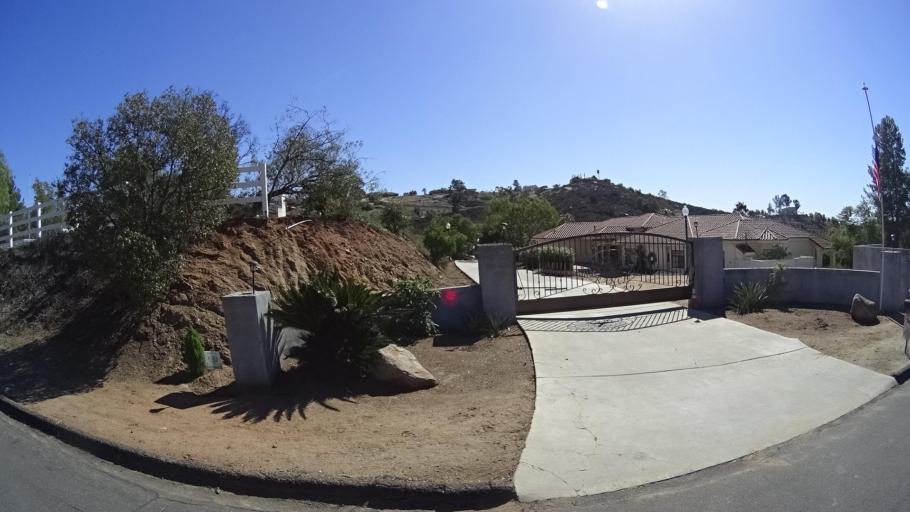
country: US
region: California
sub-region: San Diego County
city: Lakeside
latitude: 32.8651
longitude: -116.8676
